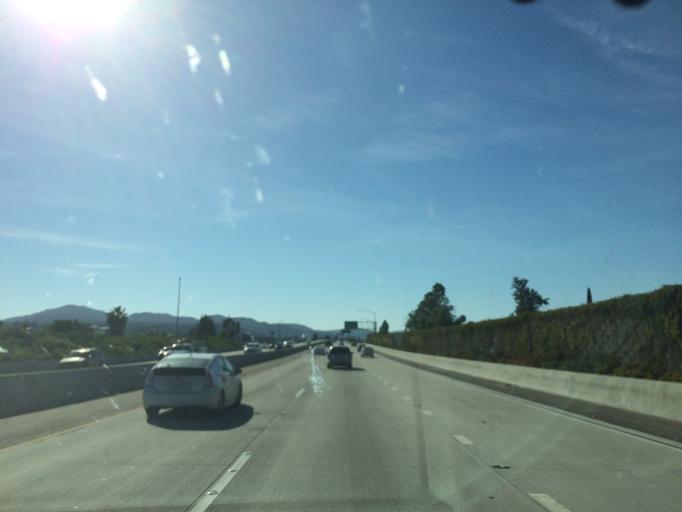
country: US
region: California
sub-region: San Diego County
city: Santee
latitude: 32.8330
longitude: -116.9766
